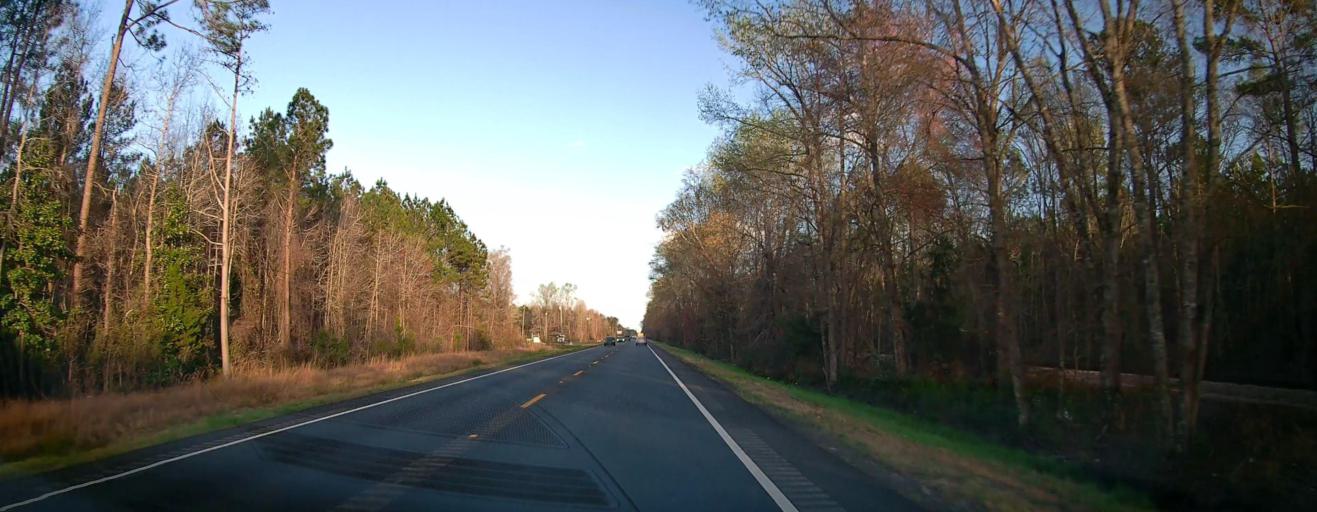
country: US
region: Georgia
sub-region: Bryan County
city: Pembroke
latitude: 32.1341
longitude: -81.5996
